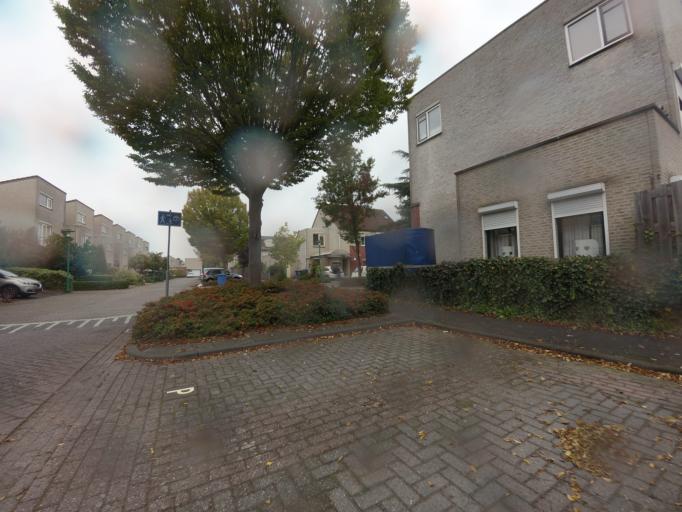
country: NL
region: North Brabant
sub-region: Gemeente Woudrichem
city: Woudrichem
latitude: 51.8382
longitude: 4.9980
